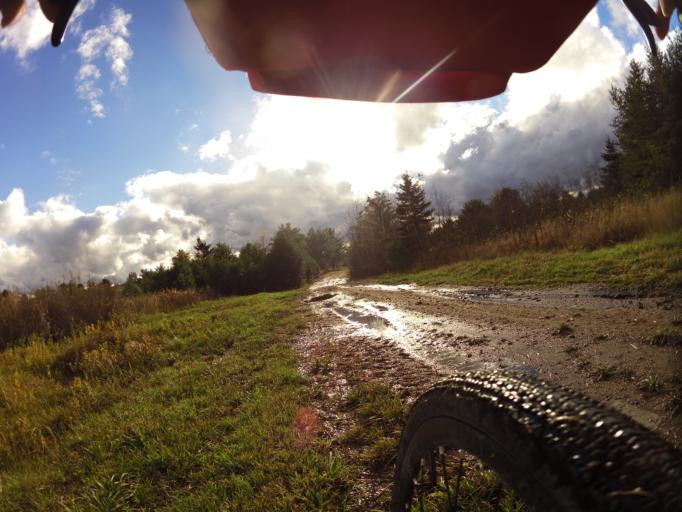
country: CA
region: Quebec
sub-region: Outaouais
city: Wakefield
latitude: 45.6643
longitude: -76.1291
